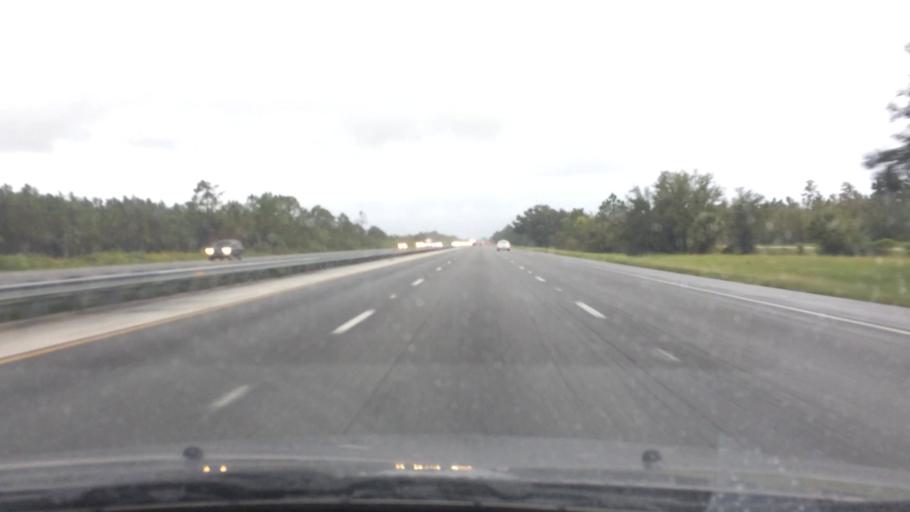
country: US
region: Florida
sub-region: Volusia County
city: Ormond-by-the-Sea
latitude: 29.3120
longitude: -81.1315
